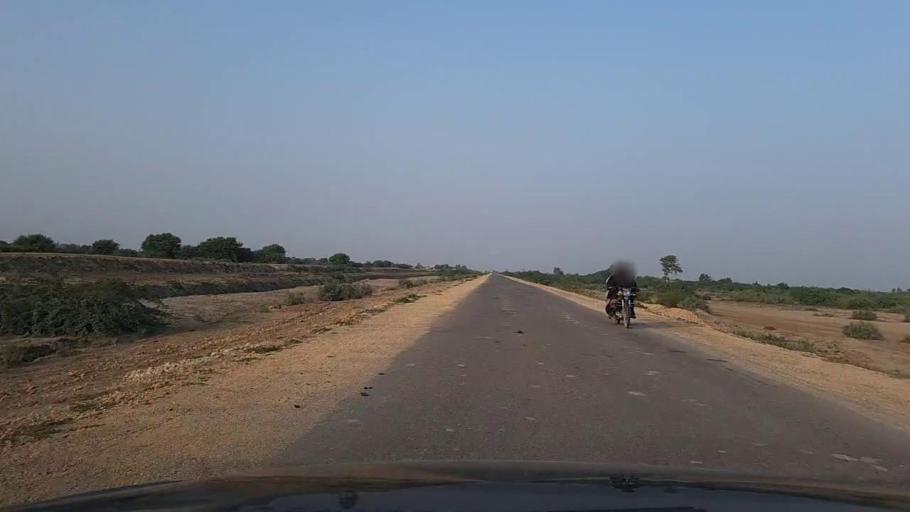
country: PK
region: Sindh
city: Mirpur Sakro
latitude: 24.4774
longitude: 67.8033
